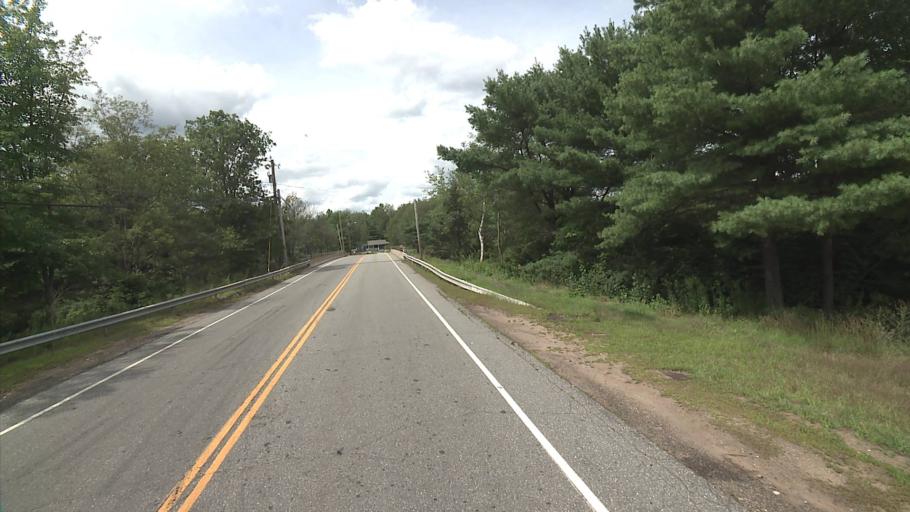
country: US
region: Massachusetts
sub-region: Hampden County
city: Holland
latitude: 42.0245
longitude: -72.1425
